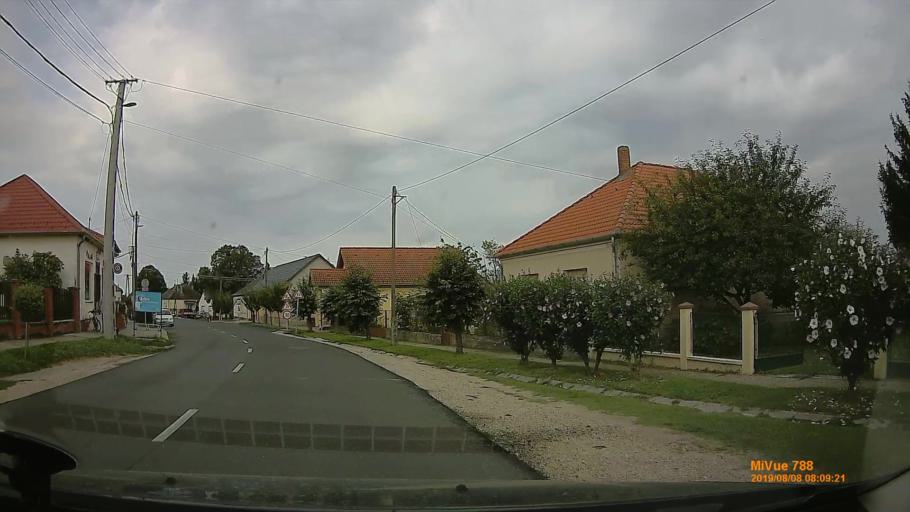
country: HU
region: Zala
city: Murakeresztur
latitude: 46.4334
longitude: 16.8994
